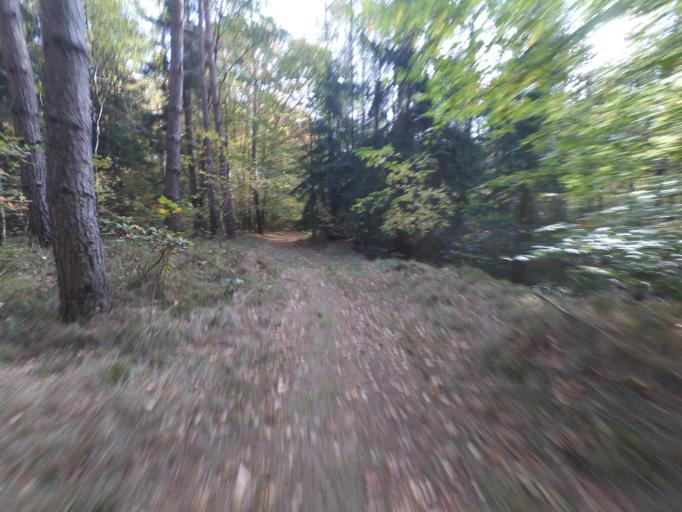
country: DE
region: Saxony
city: Radeberg
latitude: 51.0890
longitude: 13.8623
